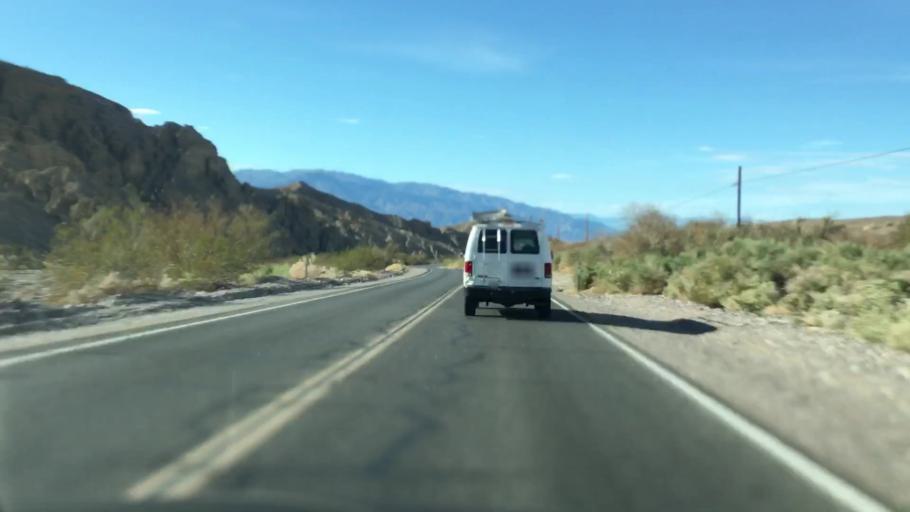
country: US
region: Nevada
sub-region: Nye County
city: Beatty
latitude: 36.4402
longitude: -116.8303
